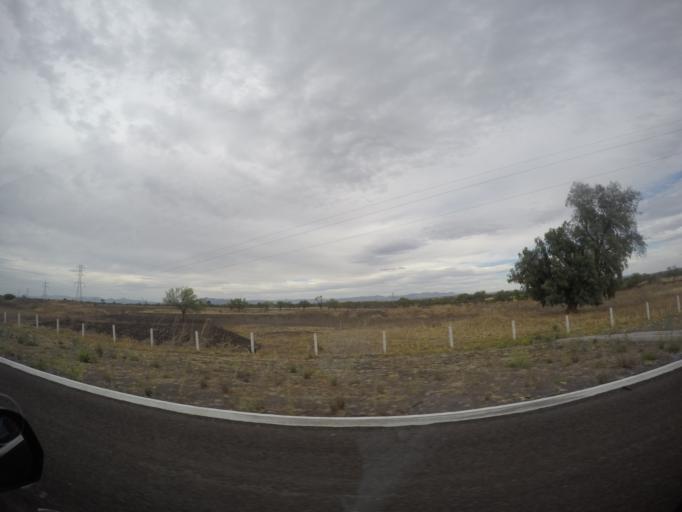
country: MX
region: Guanajuato
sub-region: Irapuato
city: Serrano
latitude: 20.8144
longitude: -101.4396
